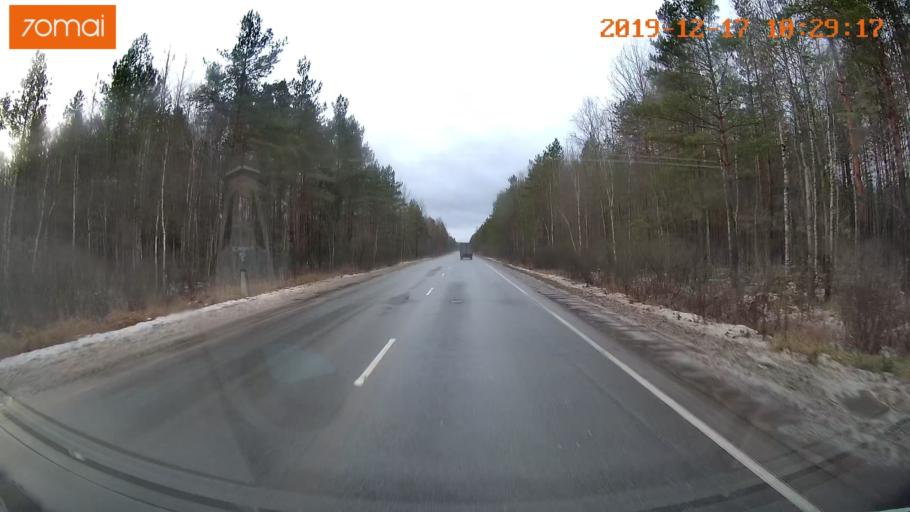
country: RU
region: Vladimir
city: Anopino
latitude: 55.6537
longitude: 40.7224
